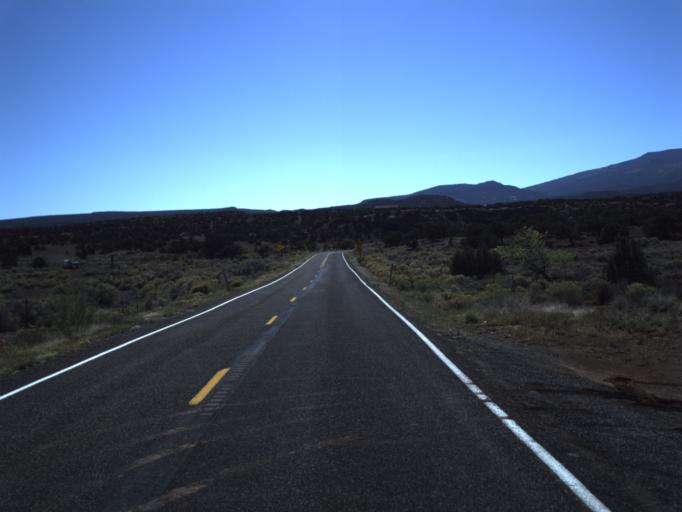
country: US
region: Utah
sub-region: Wayne County
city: Loa
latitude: 38.2923
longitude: -111.3968
